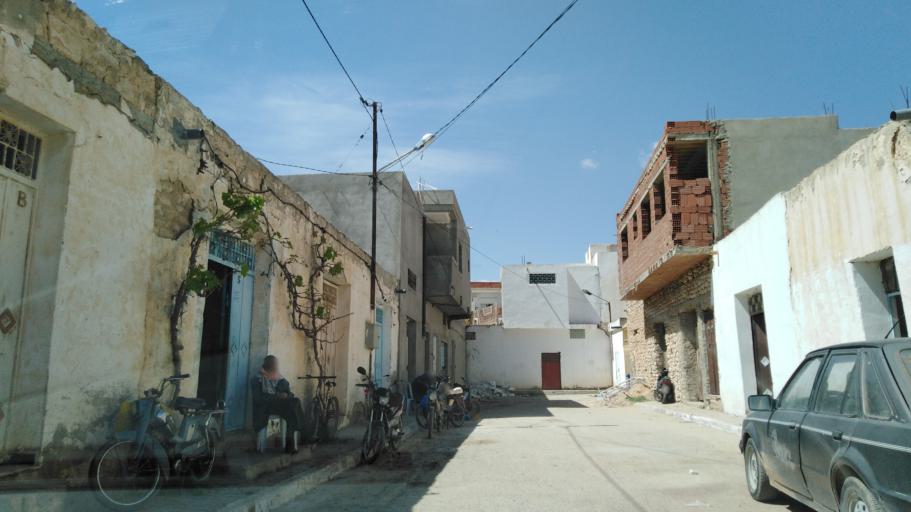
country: TN
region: Safaqis
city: Sfax
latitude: 34.7400
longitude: 10.5307
